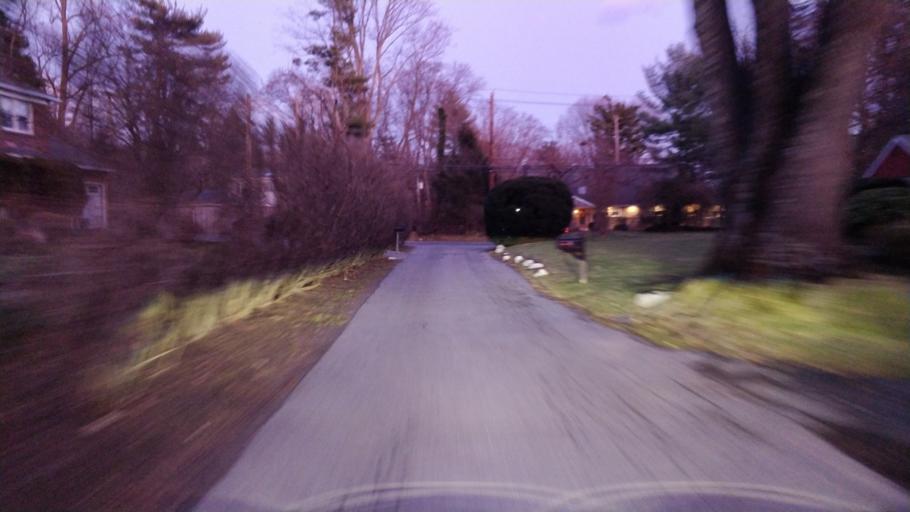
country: US
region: New York
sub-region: Nassau County
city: Glen Cove
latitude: 40.8726
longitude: -73.6408
